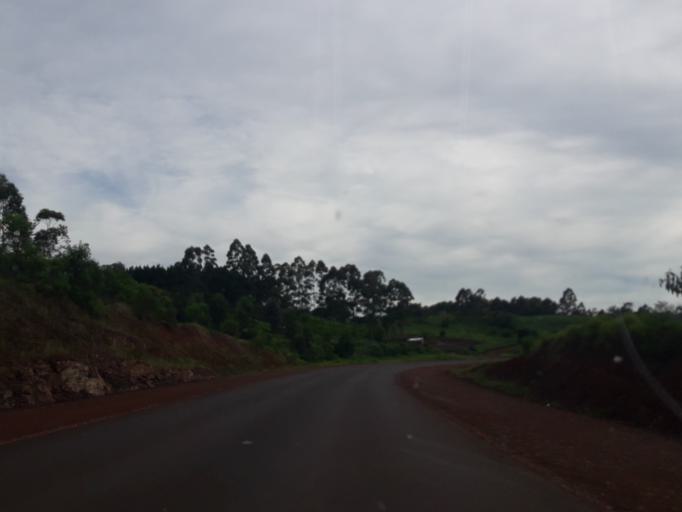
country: AR
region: Misiones
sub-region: Departamento de San Pedro
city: San Pedro
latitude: -26.5150
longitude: -53.9342
